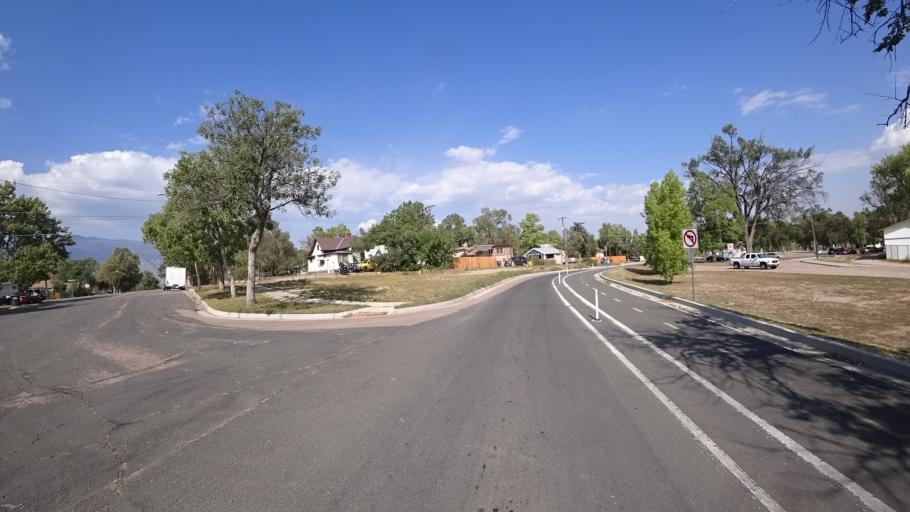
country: US
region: Colorado
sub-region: El Paso County
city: Colorado Springs
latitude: 38.8263
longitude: -104.8031
